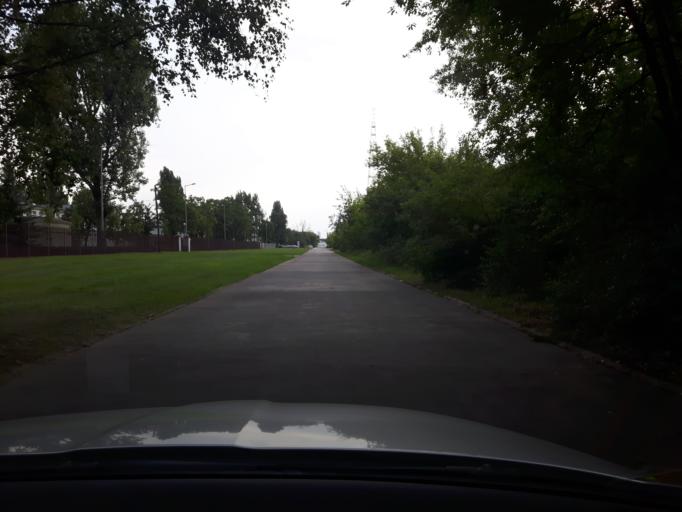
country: PL
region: Masovian Voivodeship
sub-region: Warszawa
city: Praga Poludnie
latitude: 52.2674
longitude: 21.0860
